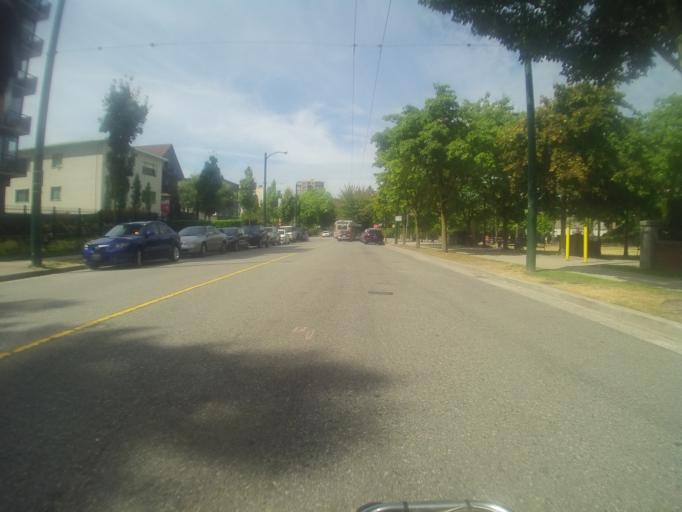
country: CA
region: British Columbia
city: West End
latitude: 49.2627
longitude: -123.1400
